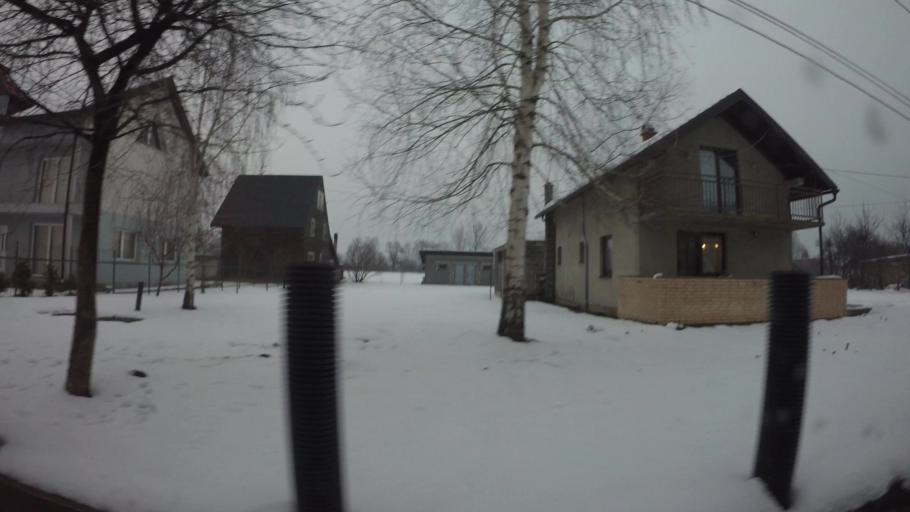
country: BA
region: Federation of Bosnia and Herzegovina
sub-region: Kanton Sarajevo
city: Sarajevo
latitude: 43.8444
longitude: 18.2976
